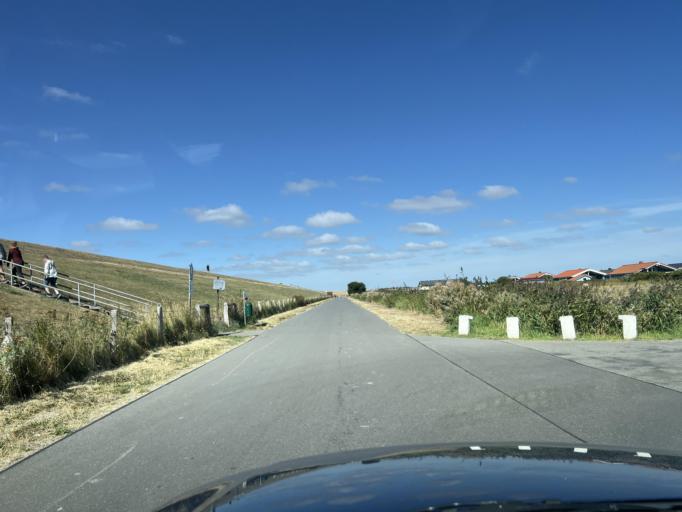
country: DE
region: Schleswig-Holstein
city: Wesselburenerkoog
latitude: 54.2489
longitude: 8.8417
